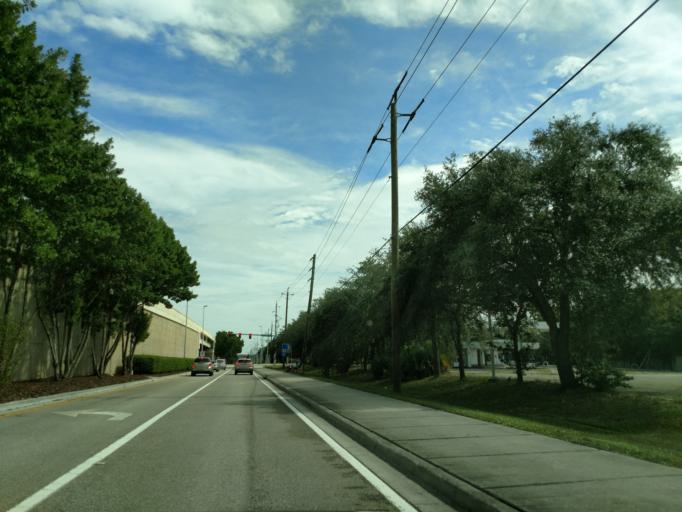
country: US
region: Florida
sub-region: Lee County
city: Harlem Heights
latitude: 26.4938
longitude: -81.9449
